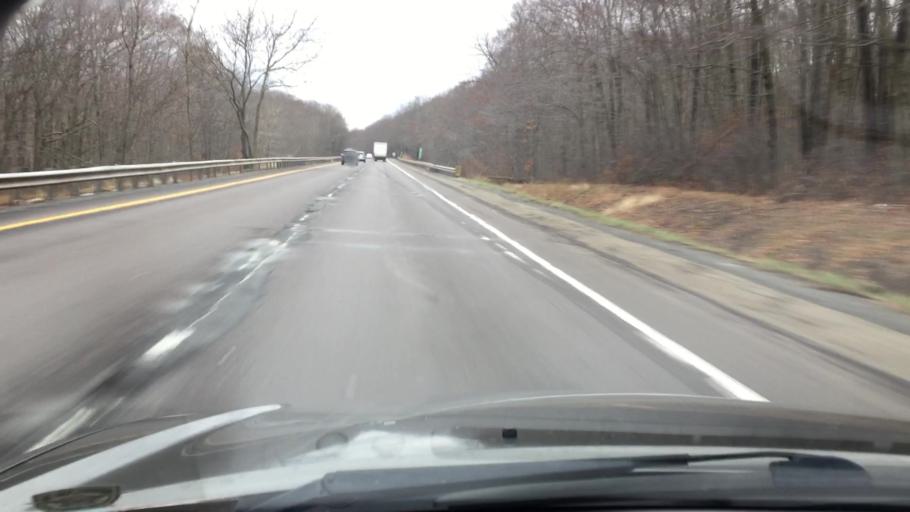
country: US
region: Pennsylvania
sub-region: Luzerne County
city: White Haven
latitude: 41.0591
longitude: -75.7364
